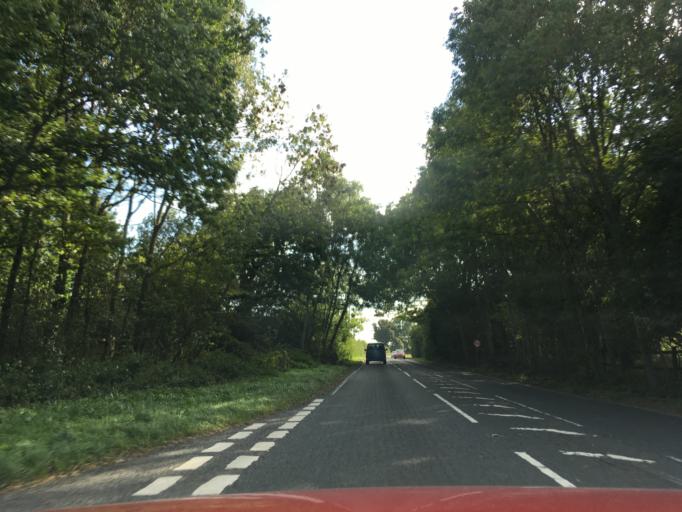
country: GB
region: England
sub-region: Hampshire
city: Old Basing
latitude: 51.1973
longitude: -1.0418
